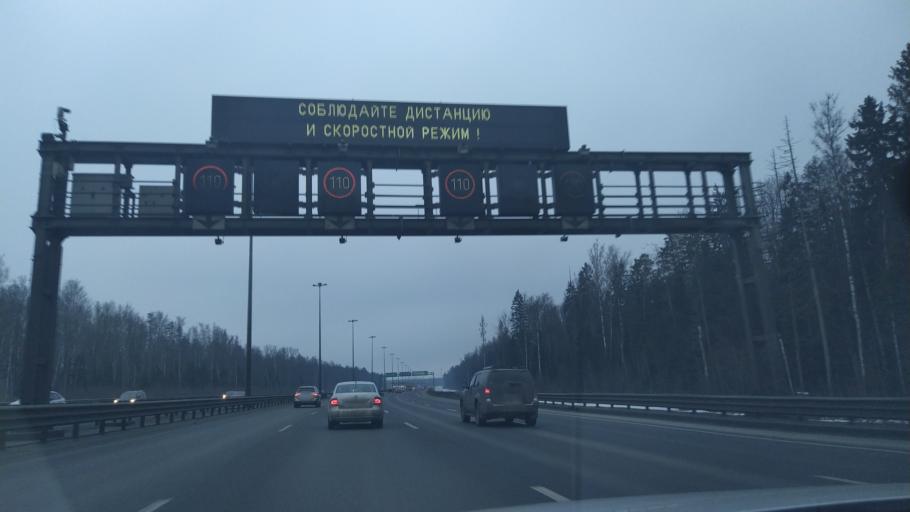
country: RU
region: Leningrad
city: Yanino Vtoroye
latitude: 59.9583
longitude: 30.5522
